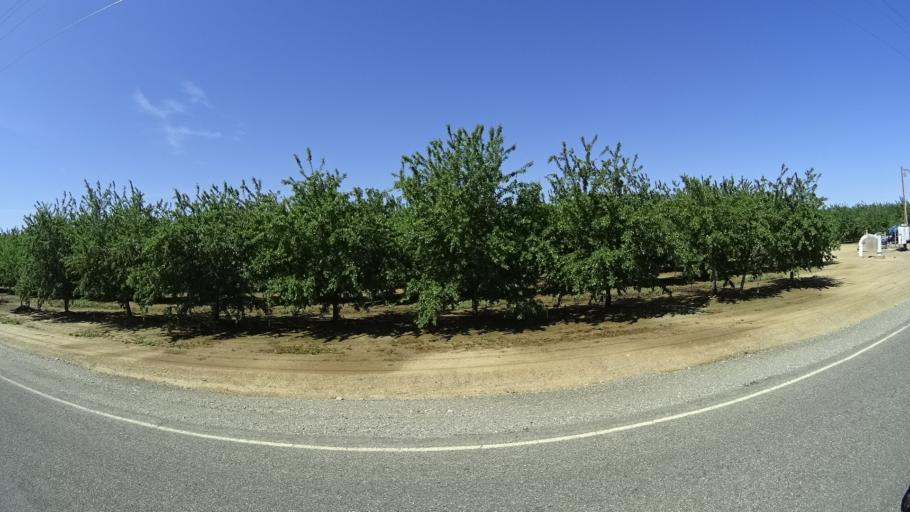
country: US
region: California
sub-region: Glenn County
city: Orland
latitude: 39.6999
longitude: -122.1780
